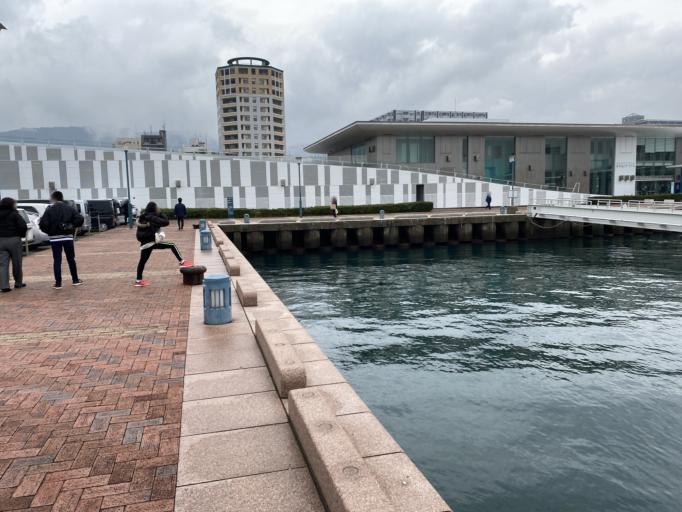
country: JP
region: Nagasaki
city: Sasebo
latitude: 33.1631
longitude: 129.7225
